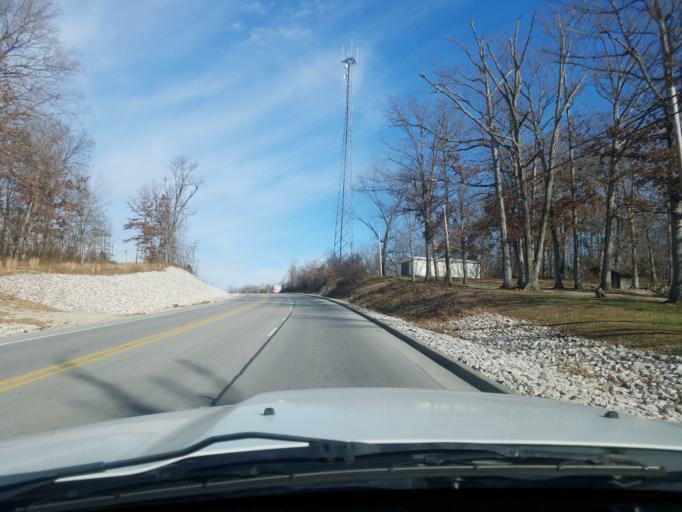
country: US
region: Indiana
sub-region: Orange County
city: Paoli
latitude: 38.5697
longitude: -86.4624
